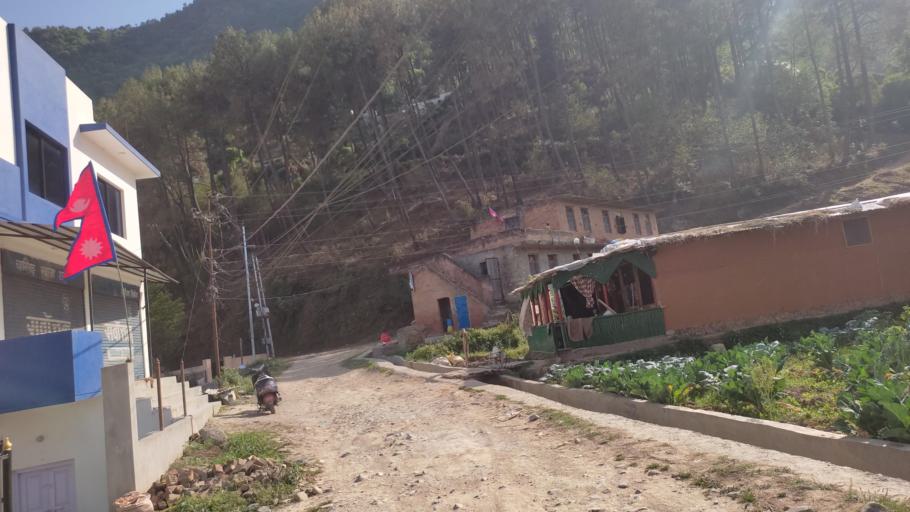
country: NP
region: Central Region
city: Kirtipur
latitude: 27.6588
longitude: 85.2647
